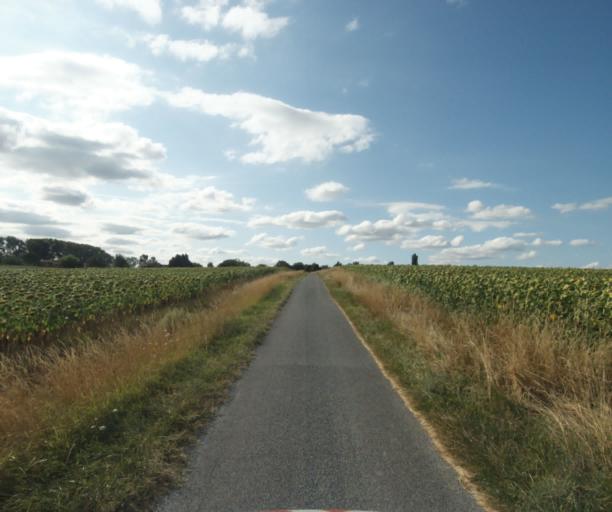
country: FR
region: Midi-Pyrenees
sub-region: Departement du Tarn
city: Puylaurens
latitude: 43.5287
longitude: 1.9938
